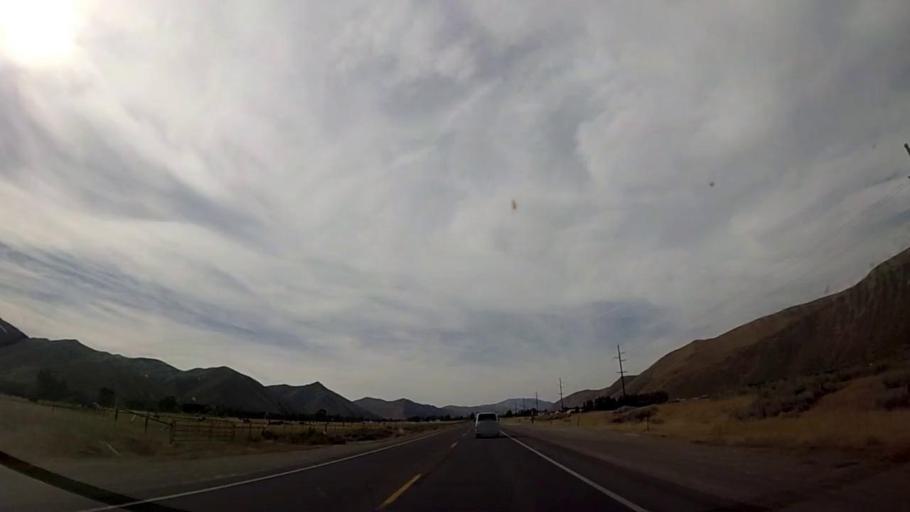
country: US
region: Idaho
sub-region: Blaine County
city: Bellevue
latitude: 43.4796
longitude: -114.2704
